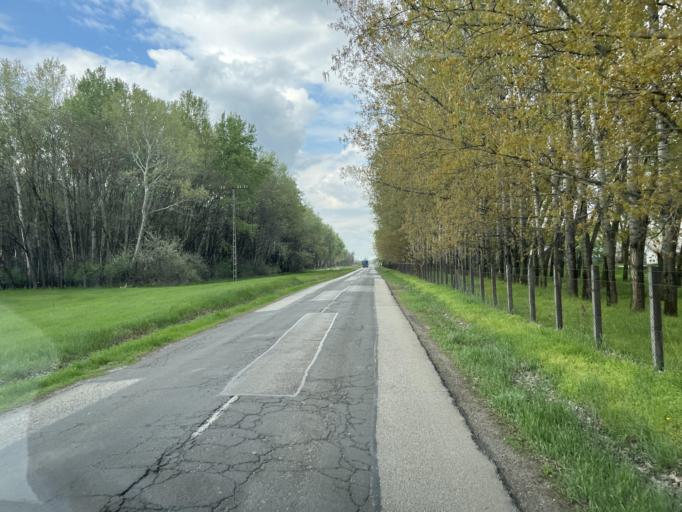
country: HU
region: Pest
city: Hernad
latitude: 47.1773
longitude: 19.4197
